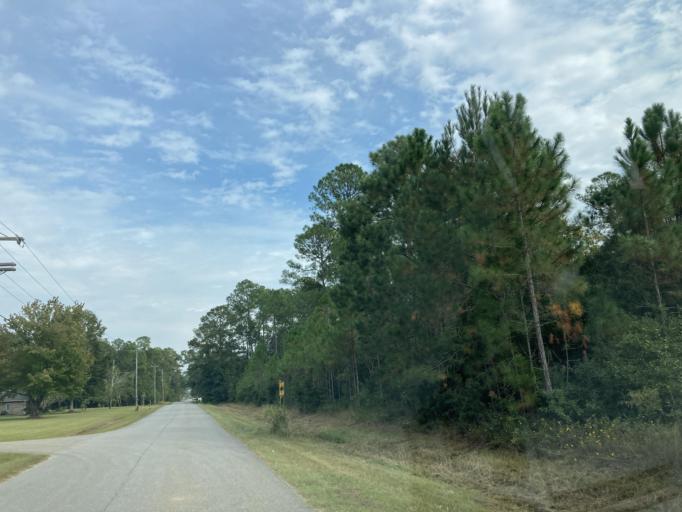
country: US
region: Mississippi
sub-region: Jackson County
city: Gulf Hills
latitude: 30.4704
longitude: -88.8430
